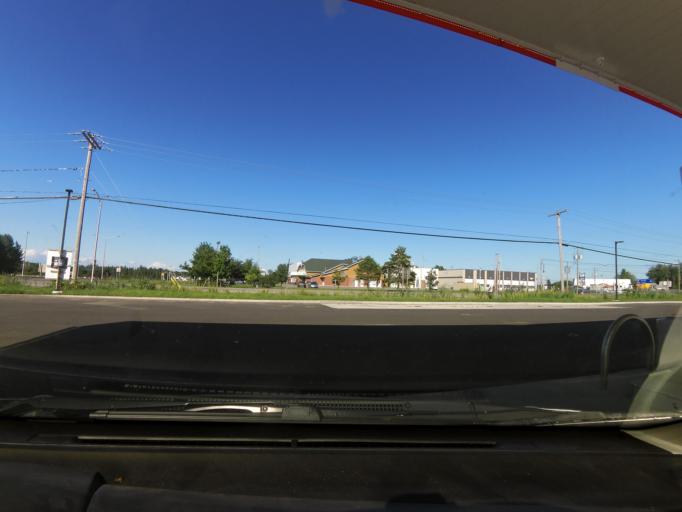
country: CA
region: Quebec
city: Sainte-Catherine
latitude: 46.2920
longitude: -72.5407
